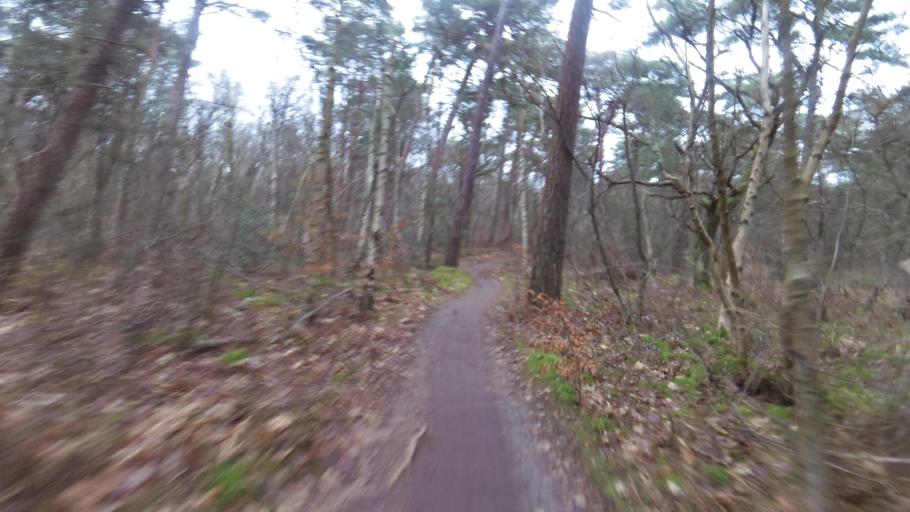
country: NL
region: North Holland
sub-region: Gemeente Bergen
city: Egmond aan Zee
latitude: 52.6816
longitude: 4.6763
